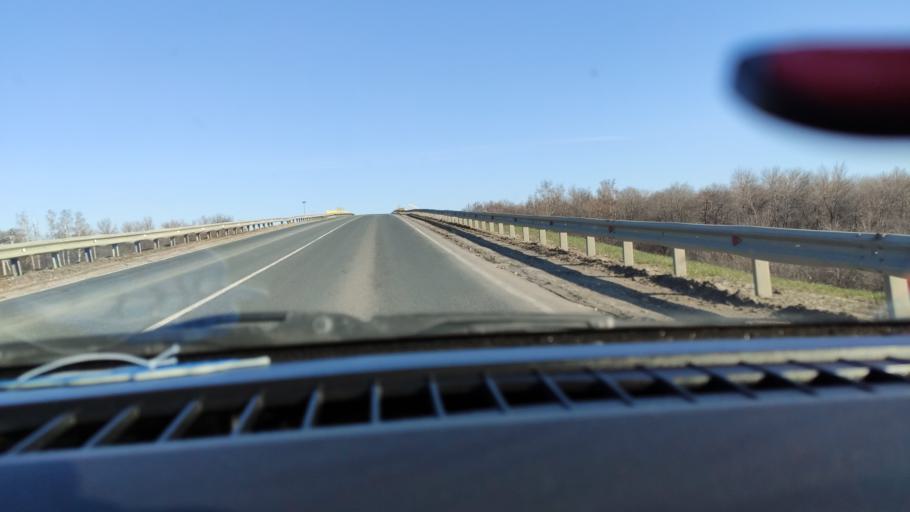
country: RU
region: Saratov
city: Dukhovnitskoye
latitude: 52.7508
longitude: 48.2483
